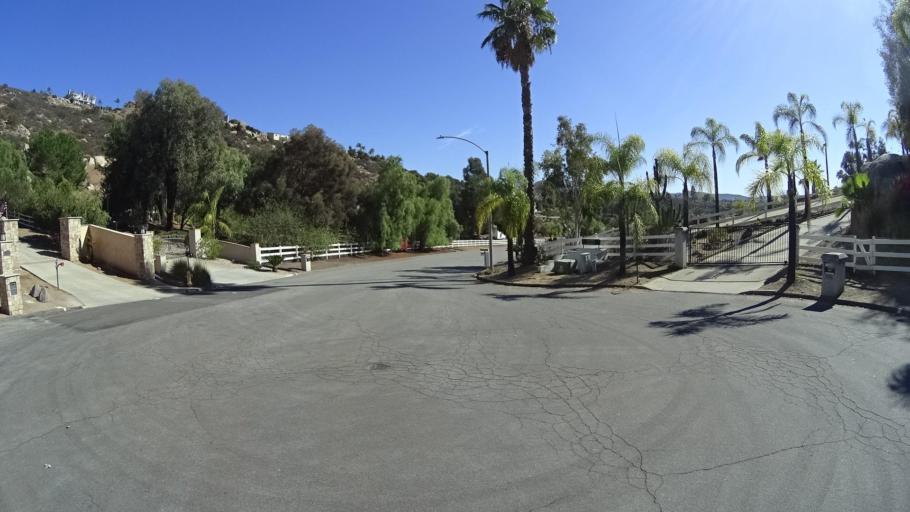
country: US
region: California
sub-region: San Diego County
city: Lakeside
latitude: 32.8699
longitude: -116.8714
